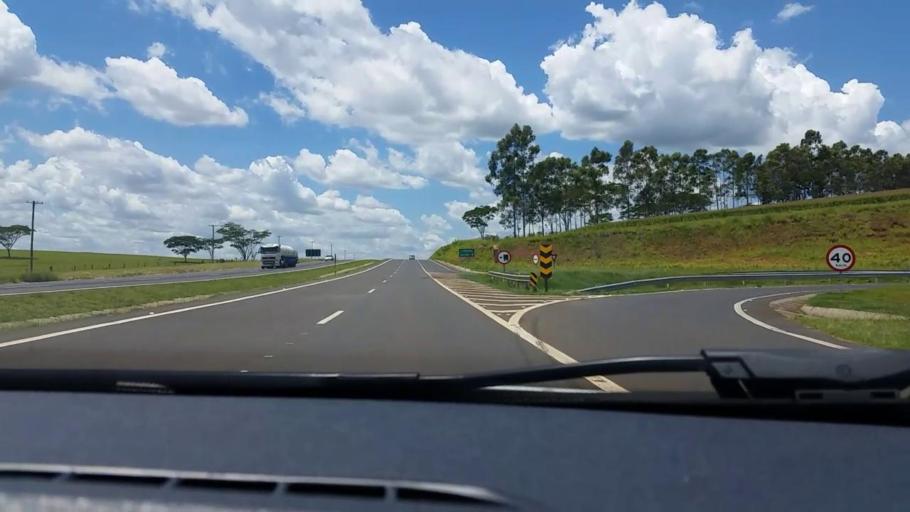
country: BR
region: Sao Paulo
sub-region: Bauru
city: Bauru
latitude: -22.4237
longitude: -49.1231
